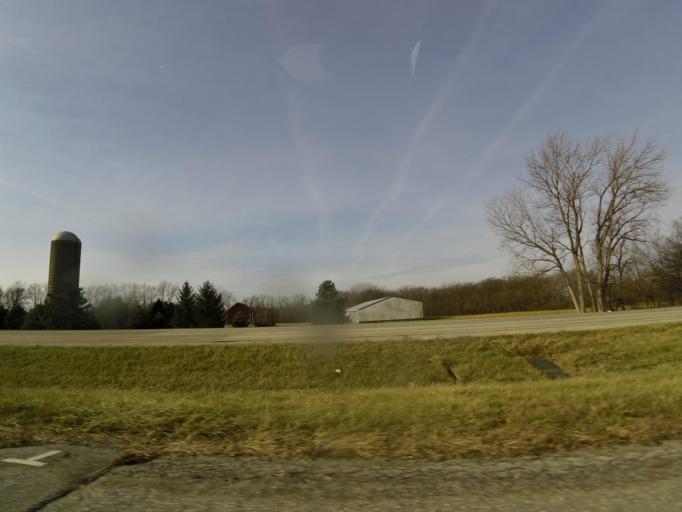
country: US
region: Illinois
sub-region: De Witt County
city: Clinton
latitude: 40.1512
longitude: -88.9854
